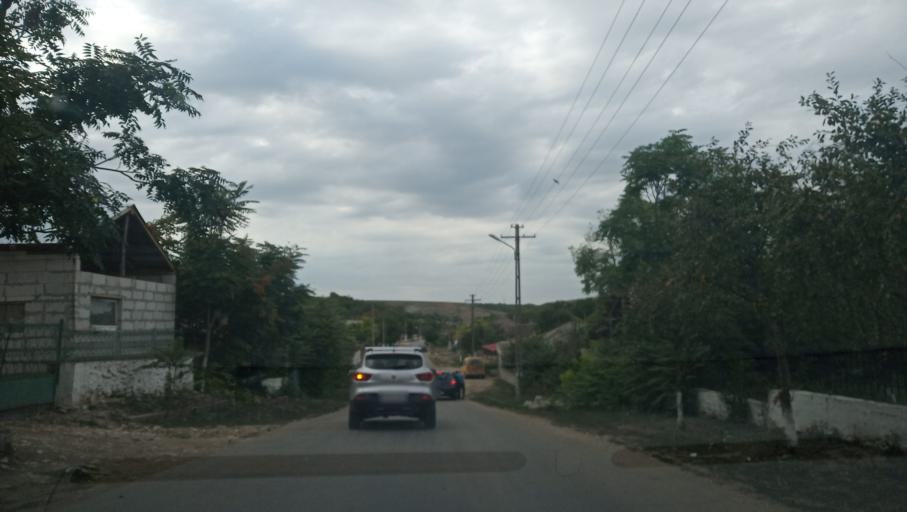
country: RO
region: Constanta
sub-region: Comuna Dumbraveni
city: Dumbraveni
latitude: 43.9895
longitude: 28.0104
